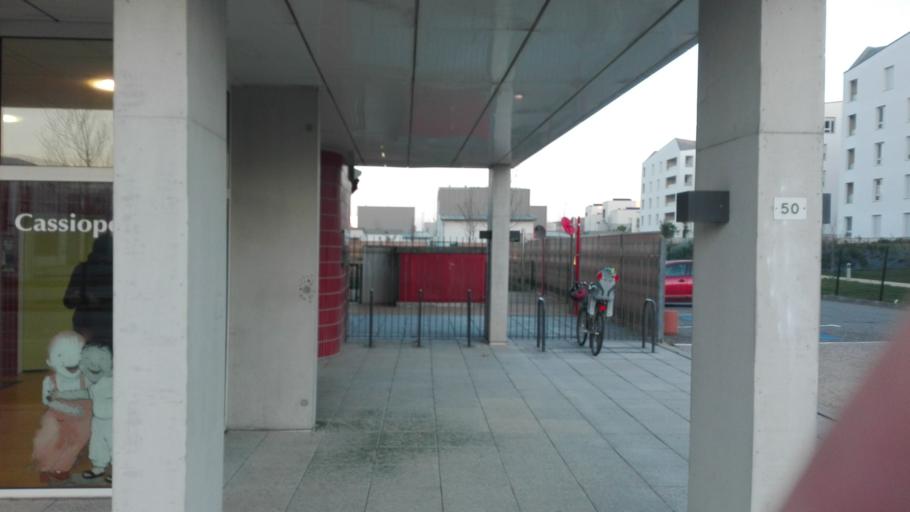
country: FR
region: Midi-Pyrenees
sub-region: Departement de la Haute-Garonne
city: Beauzelle
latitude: 43.6534
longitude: 1.3690
